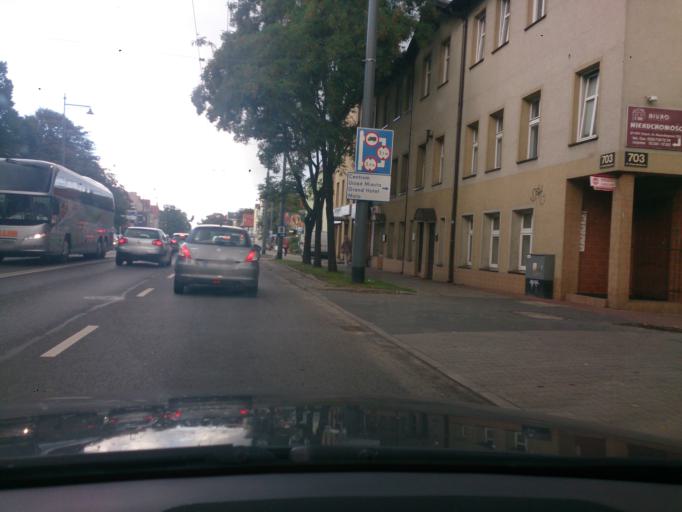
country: PL
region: Pomeranian Voivodeship
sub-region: Sopot
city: Sopot
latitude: 54.4334
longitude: 18.5618
